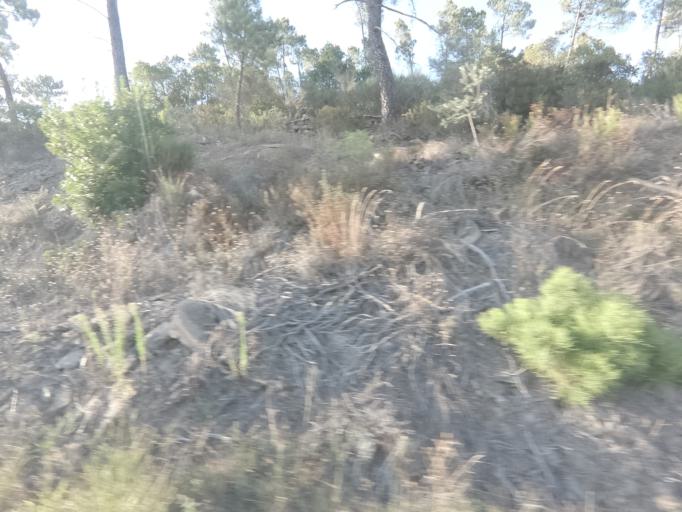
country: PT
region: Vila Real
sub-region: Sabrosa
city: Sabrosa
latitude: 41.2632
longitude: -7.5642
